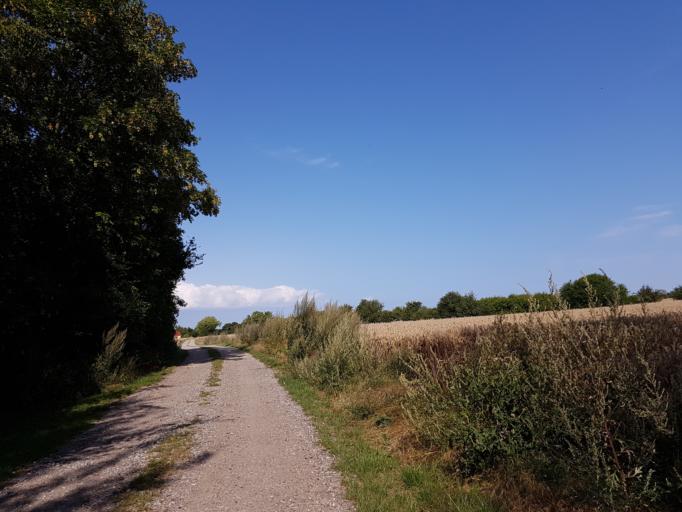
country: DK
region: Zealand
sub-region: Guldborgsund Kommune
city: Nykobing Falster
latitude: 54.5706
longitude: 11.9410
